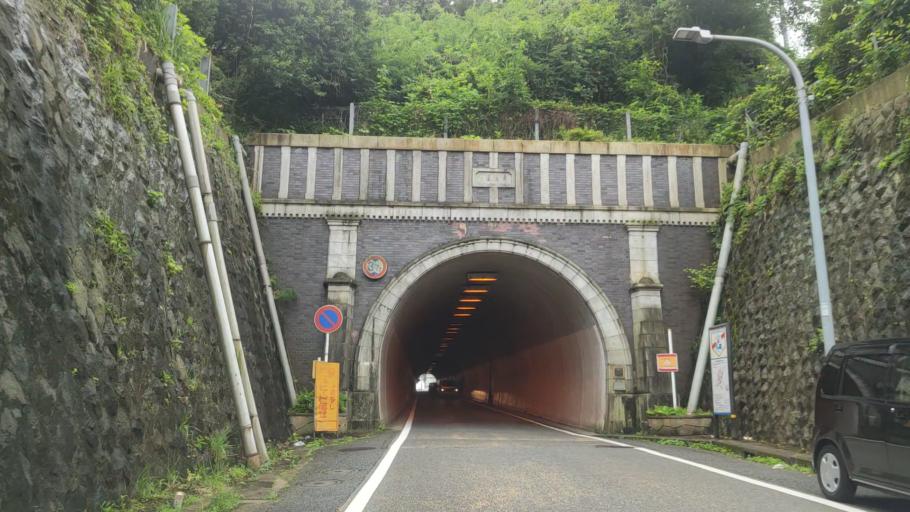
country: JP
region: Kanagawa
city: Yokohama
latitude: 35.4451
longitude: 139.6020
